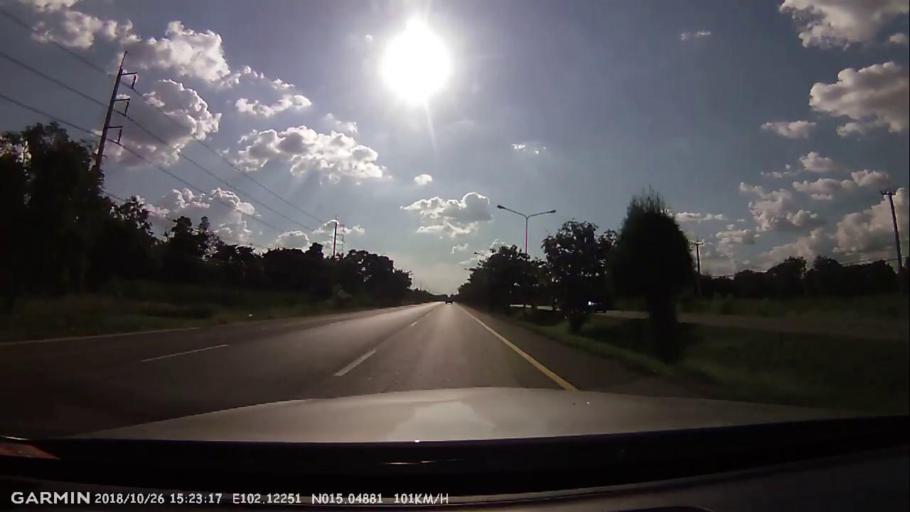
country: TH
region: Nakhon Ratchasima
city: Nakhon Ratchasima
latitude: 15.0488
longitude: 102.1225
